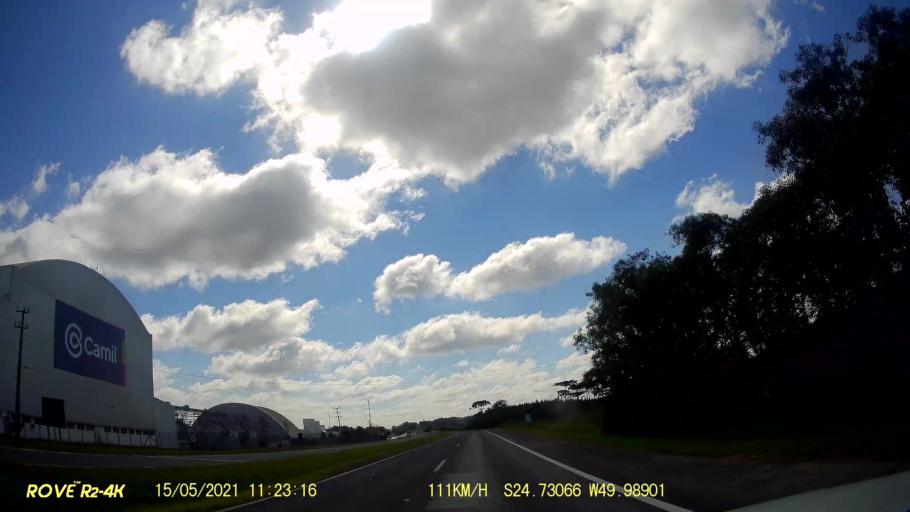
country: BR
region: Parana
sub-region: Castro
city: Castro
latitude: -24.7308
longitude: -49.9893
